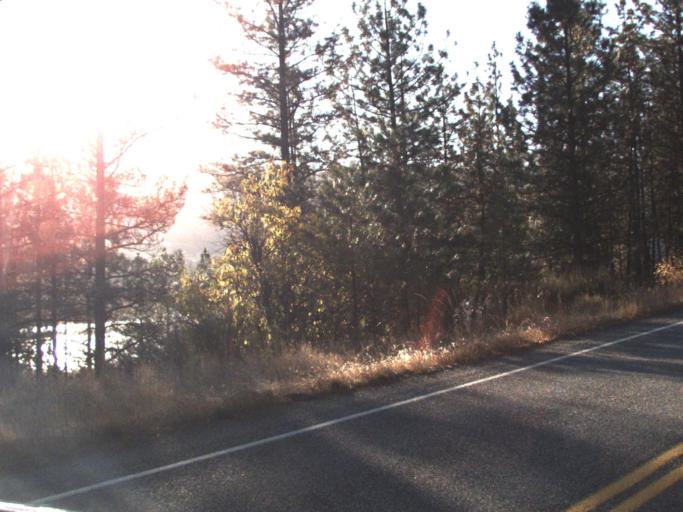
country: US
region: Washington
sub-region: Okanogan County
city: Coulee Dam
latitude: 48.0311
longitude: -118.6744
